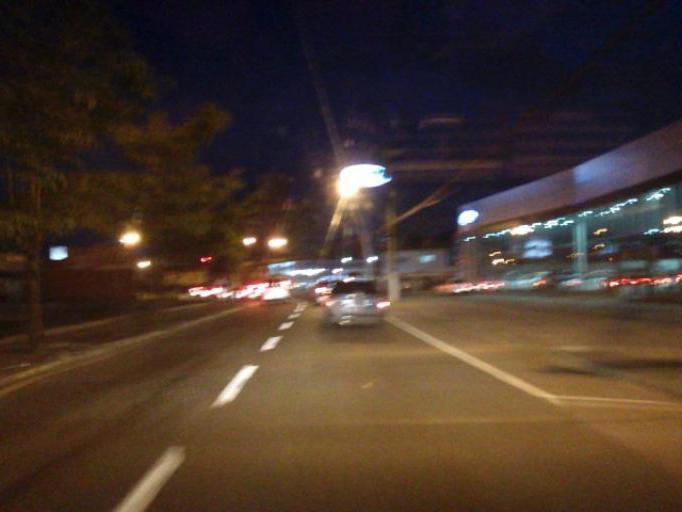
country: BR
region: Santa Catarina
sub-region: Itajai
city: Itajai
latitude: -26.9018
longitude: -48.6717
